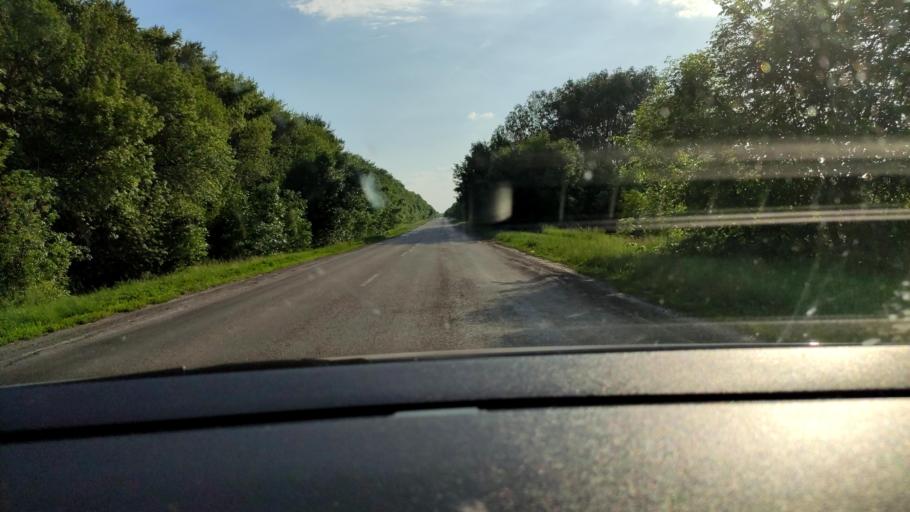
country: RU
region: Voronezj
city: Panino
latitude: 51.5806
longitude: 39.9427
